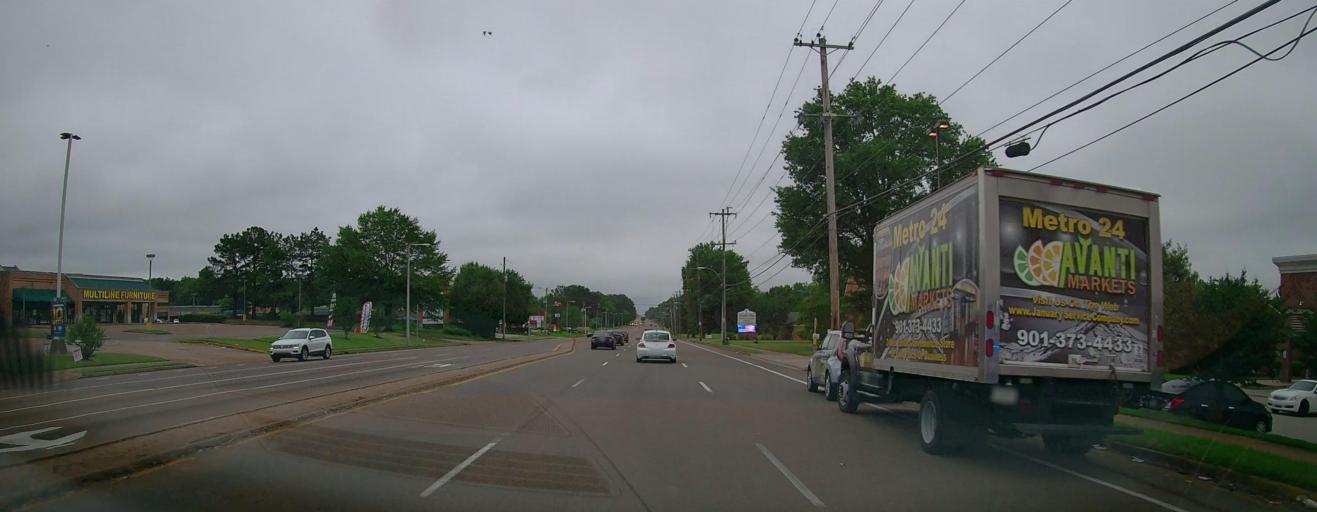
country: US
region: Mississippi
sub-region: De Soto County
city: Olive Branch
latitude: 35.0204
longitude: -89.8313
